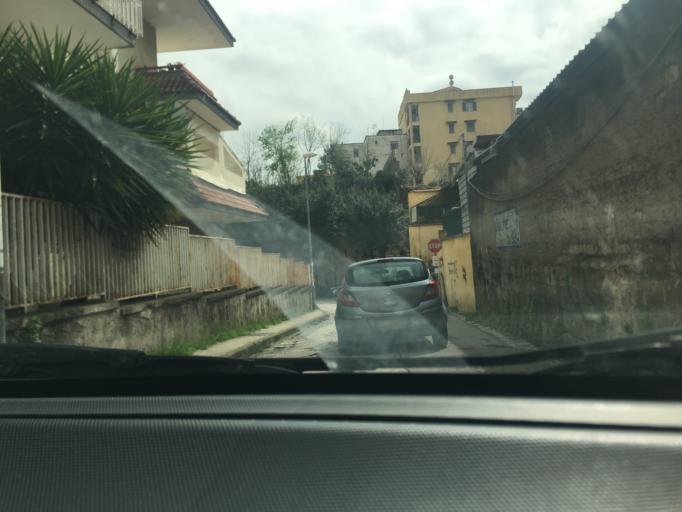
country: IT
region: Campania
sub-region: Provincia di Napoli
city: Marano di Napoli
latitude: 40.8961
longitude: 14.1845
